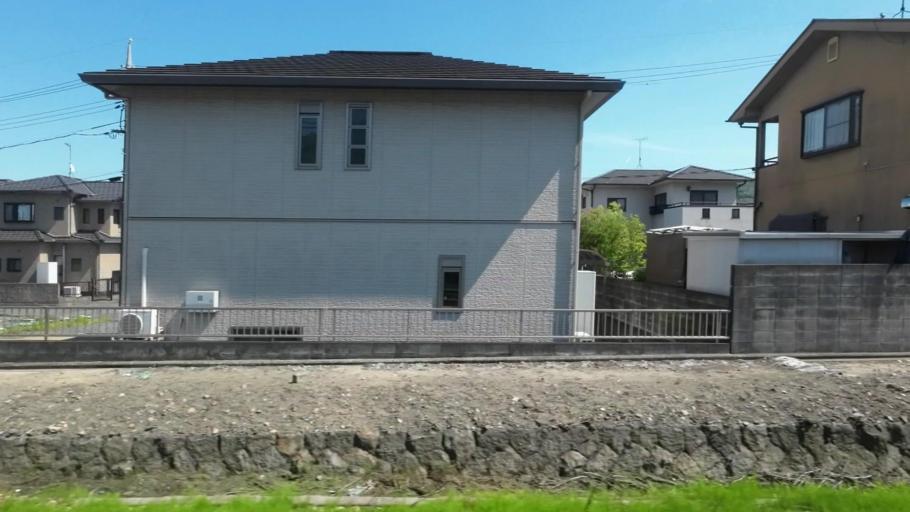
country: JP
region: Hiroshima
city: Fukuyama
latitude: 34.4682
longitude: 133.2987
